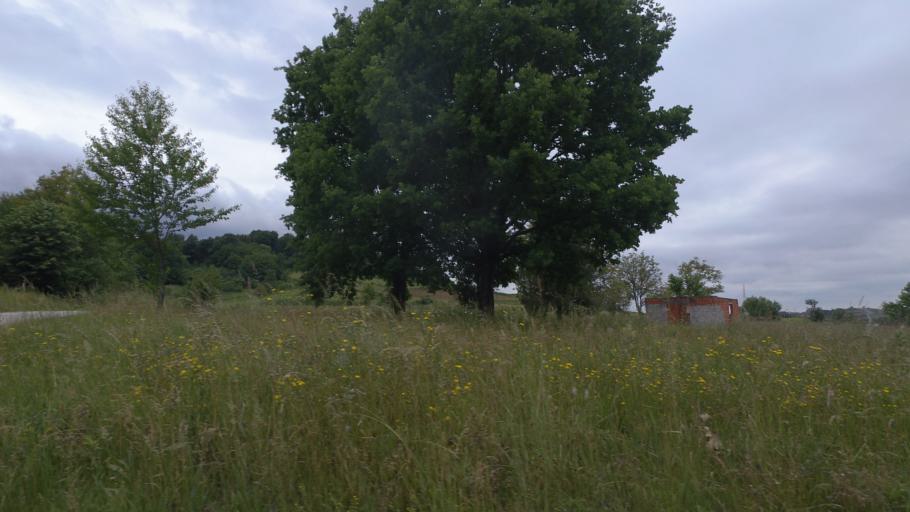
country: HR
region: Karlovacka
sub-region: Grad Karlovac
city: Karlovac
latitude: 45.4381
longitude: 15.5482
